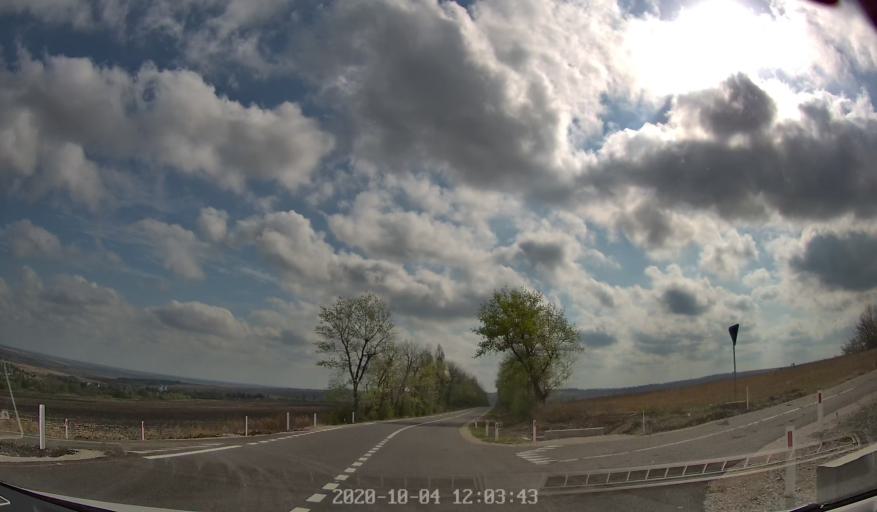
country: MD
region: Rezina
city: Saharna
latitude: 47.6101
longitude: 28.9321
